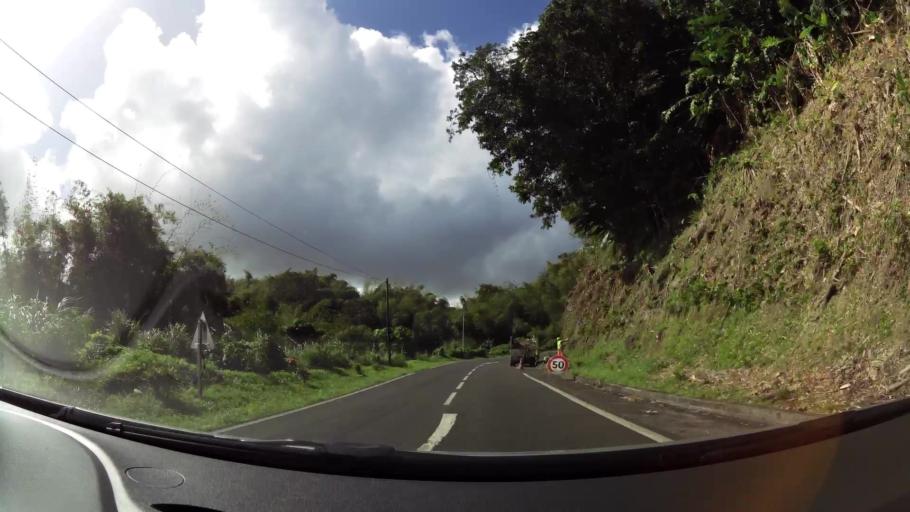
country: MQ
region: Martinique
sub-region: Martinique
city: Basse-Pointe
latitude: 14.8309
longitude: -61.1014
